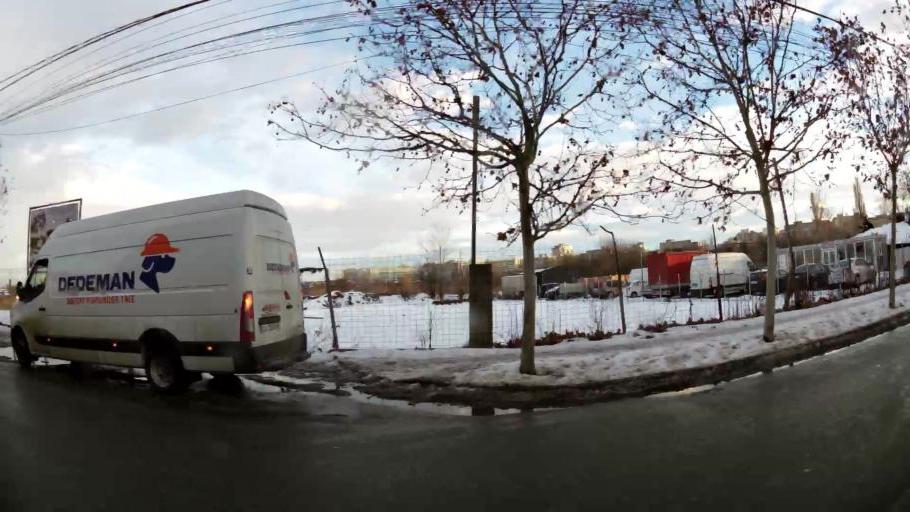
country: RO
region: Ilfov
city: Dobroesti
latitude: 44.4469
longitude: 26.1712
